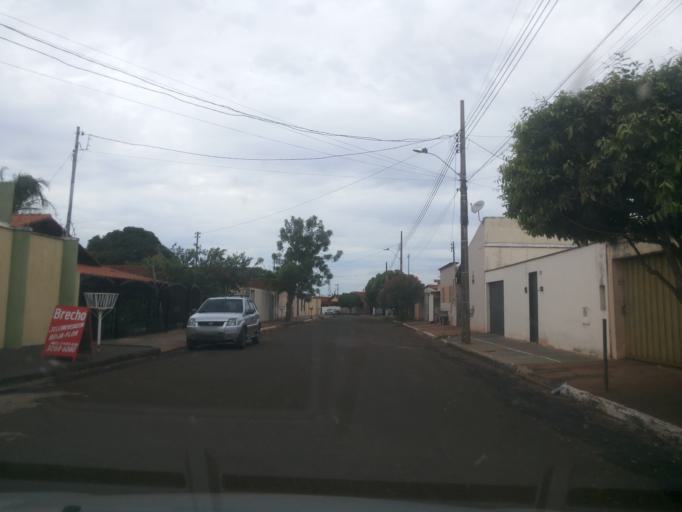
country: BR
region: Minas Gerais
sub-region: Ituiutaba
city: Ituiutaba
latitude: -18.9754
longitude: -49.4772
